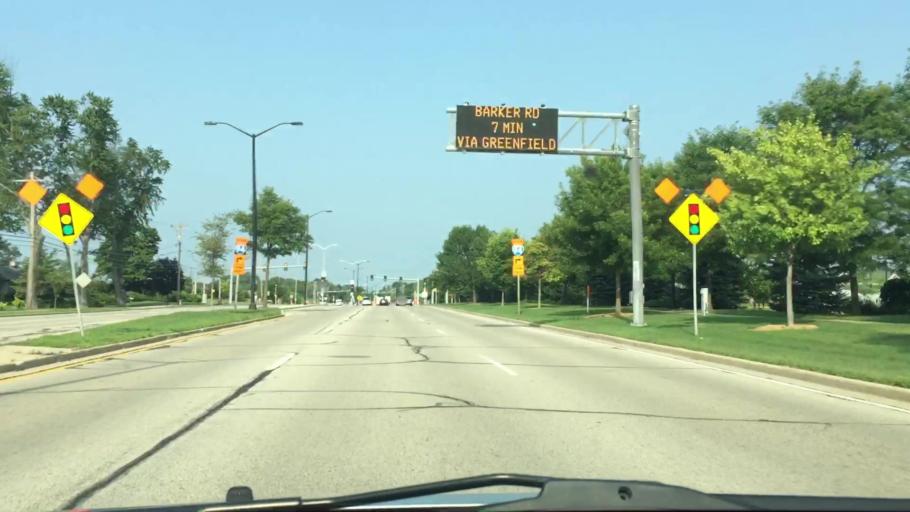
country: US
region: Wisconsin
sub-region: Waukesha County
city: Elm Grove
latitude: 43.0168
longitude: -88.1010
